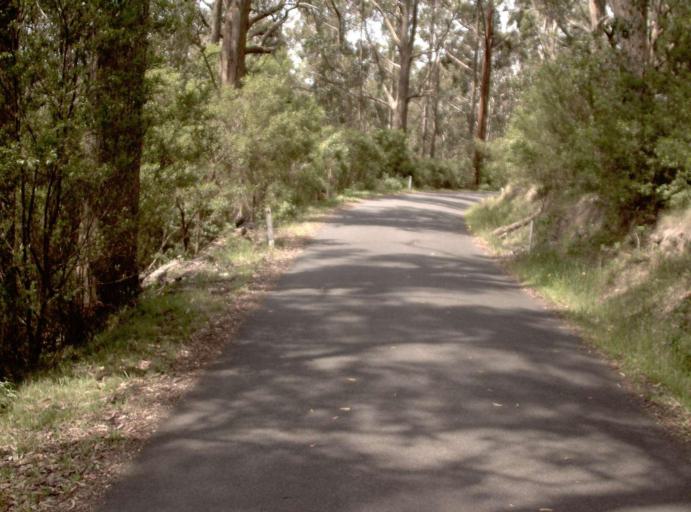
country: AU
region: Victoria
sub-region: Latrobe
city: Traralgon
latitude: -38.3670
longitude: 146.6972
